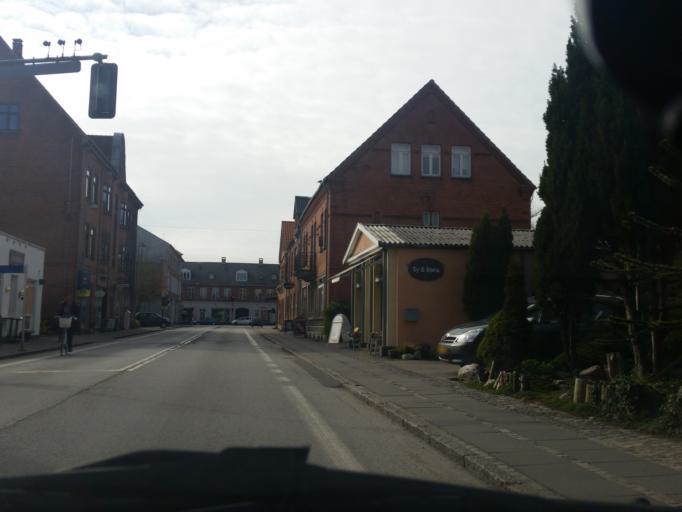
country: DK
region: Zealand
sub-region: Soro Kommune
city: Soro
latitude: 55.4344
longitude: 11.5595
